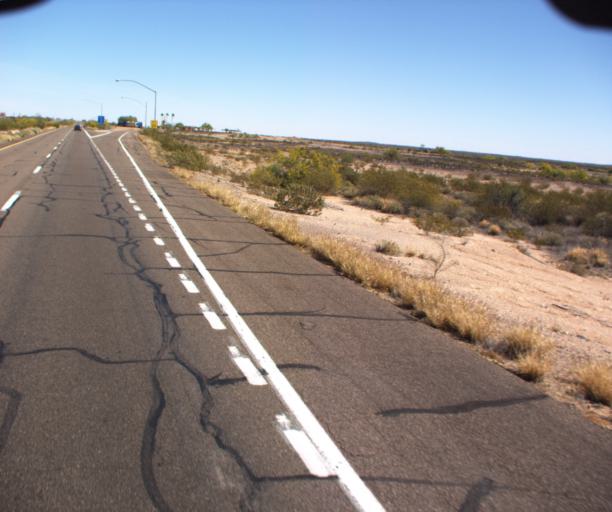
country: US
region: Arizona
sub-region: Maricopa County
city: Gila Bend
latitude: 32.8484
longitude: -113.2700
